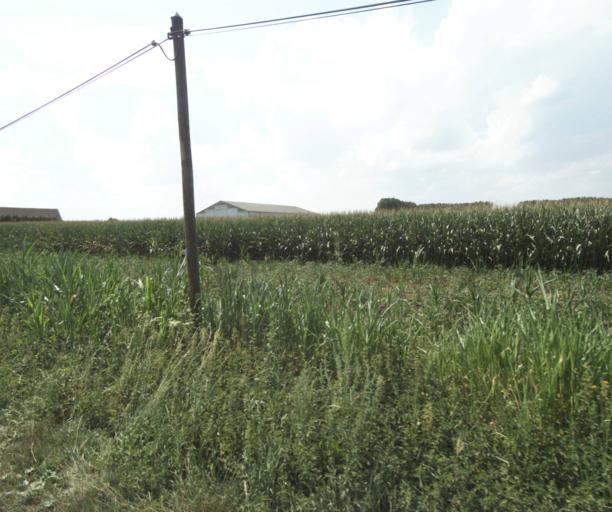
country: FR
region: Nord-Pas-de-Calais
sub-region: Departement du Nord
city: Quesnoy-sur-Deule
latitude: 50.7237
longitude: 2.9853
